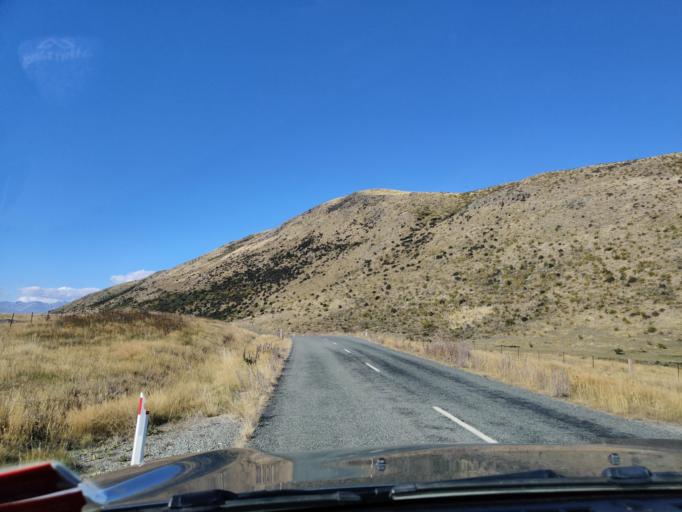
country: NZ
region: Canterbury
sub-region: Timaru District
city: Pleasant Point
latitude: -43.9887
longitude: 170.4525
